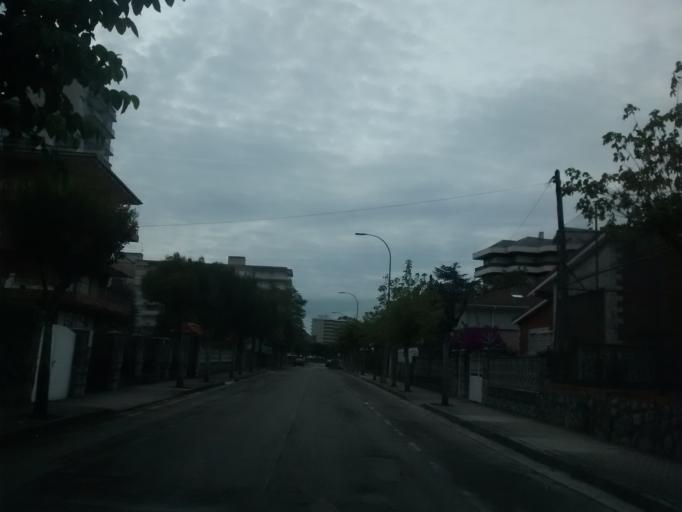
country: ES
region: Cantabria
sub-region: Provincia de Cantabria
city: Laredo
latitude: 43.4100
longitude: -3.4290
